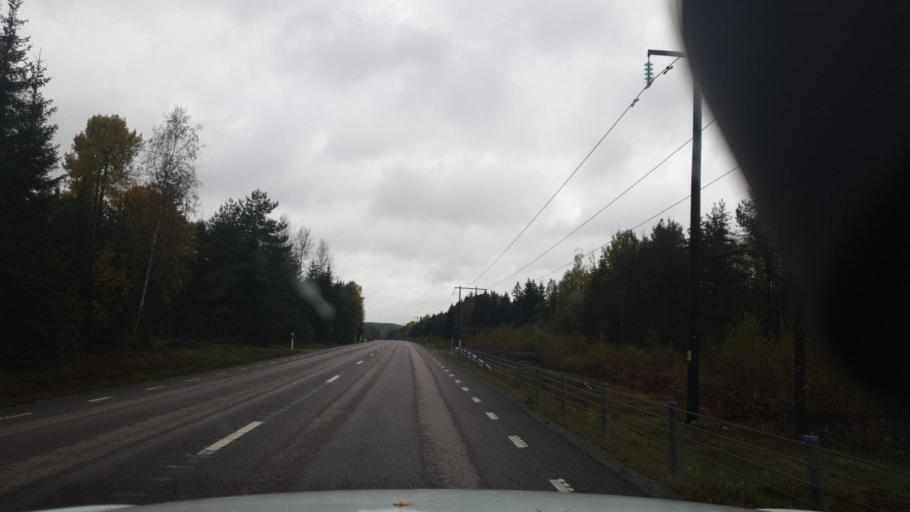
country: SE
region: Vaermland
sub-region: Karlstads Kommun
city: Edsvalla
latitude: 59.4351
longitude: 13.2011
